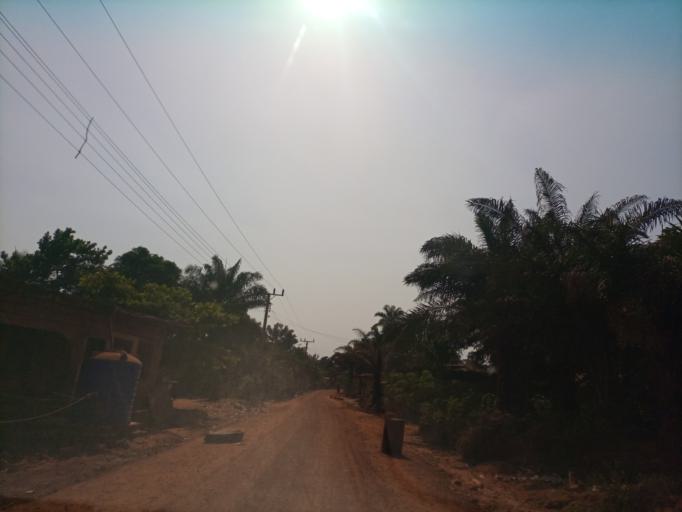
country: NG
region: Enugu
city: Aku
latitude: 6.7093
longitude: 7.3391
